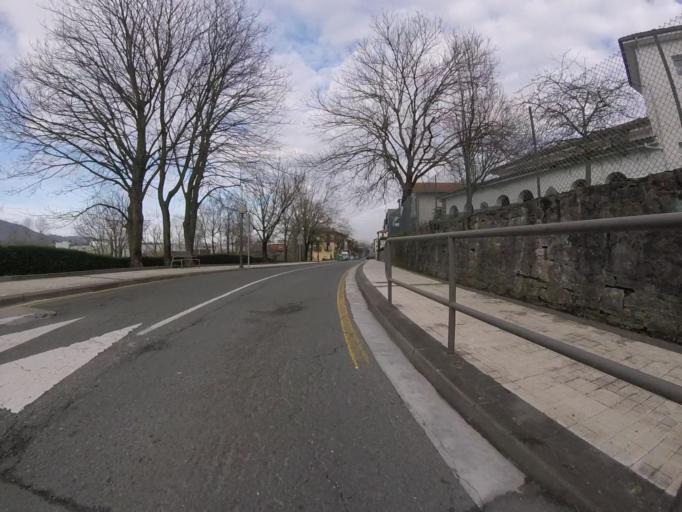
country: ES
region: Basque Country
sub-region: Provincia de Guipuzcoa
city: Irun
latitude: 43.3288
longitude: -1.8192
